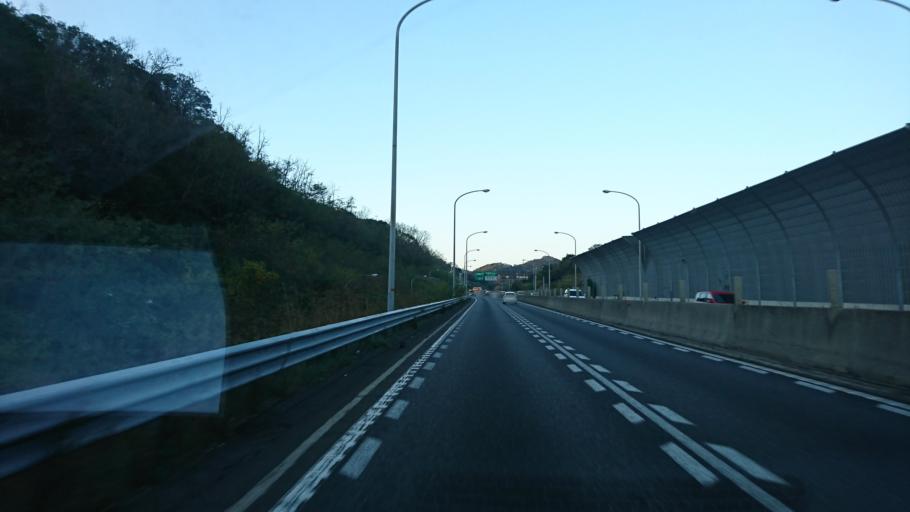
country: JP
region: Hyogo
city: Kobe
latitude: 34.6546
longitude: 135.1119
